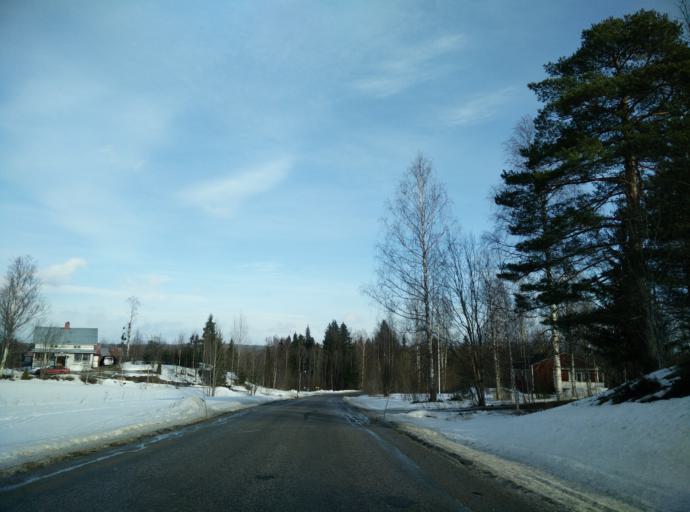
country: SE
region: Vaesternorrland
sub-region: Sundsvalls Kommun
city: Njurundabommen
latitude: 62.2188
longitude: 17.3040
